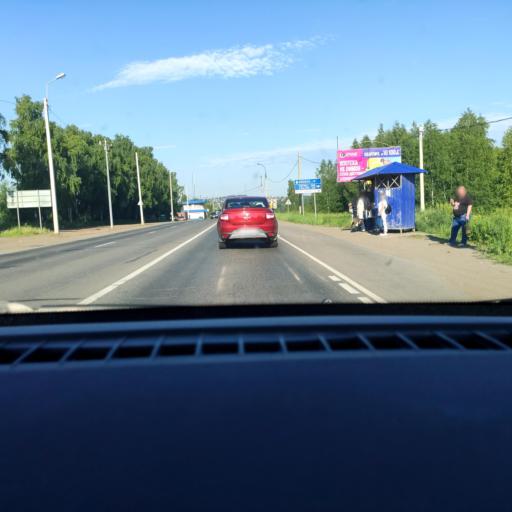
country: RU
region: Udmurtiya
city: Khokhryaki
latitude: 56.9143
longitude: 53.3973
